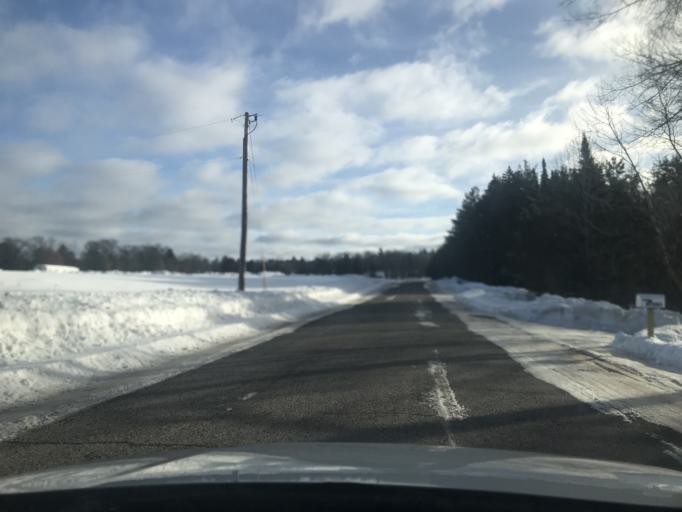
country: US
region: Wisconsin
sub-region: Marinette County
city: Niagara
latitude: 45.6264
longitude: -87.9721
